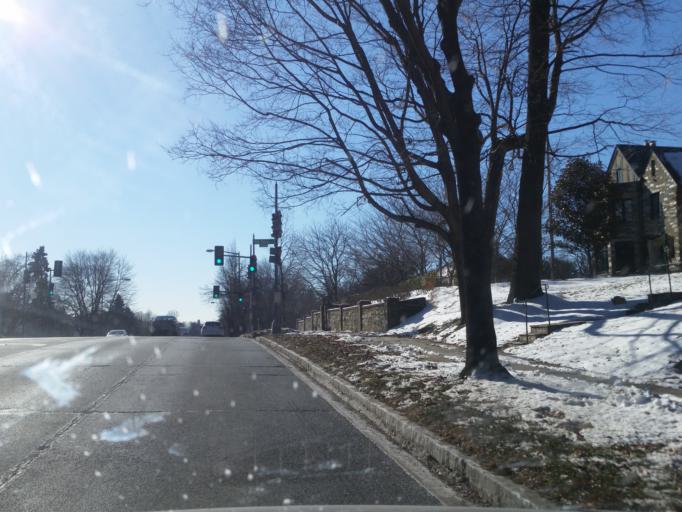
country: US
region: Maryland
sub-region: Montgomery County
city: Silver Spring
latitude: 38.9703
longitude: -77.0364
